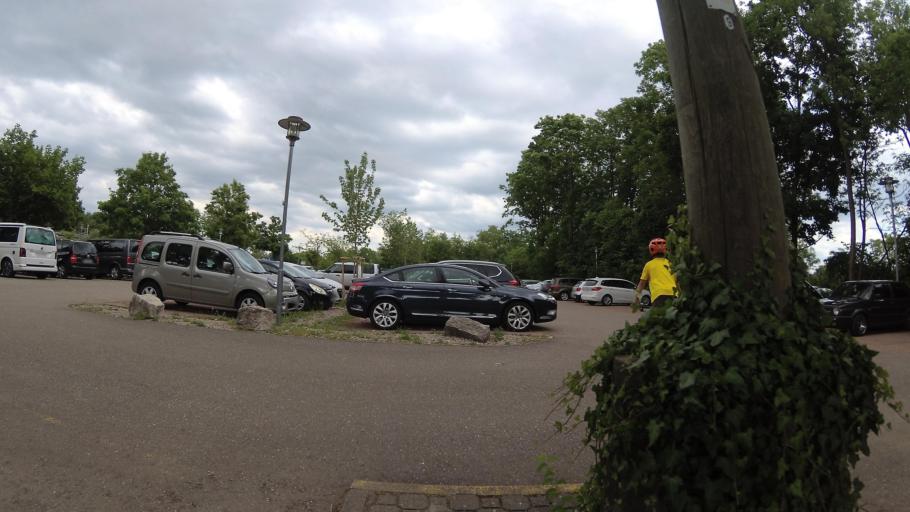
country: DE
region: Baden-Wuerttemberg
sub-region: Freiburg Region
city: Weil am Rhein
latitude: 47.5860
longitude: 7.6163
